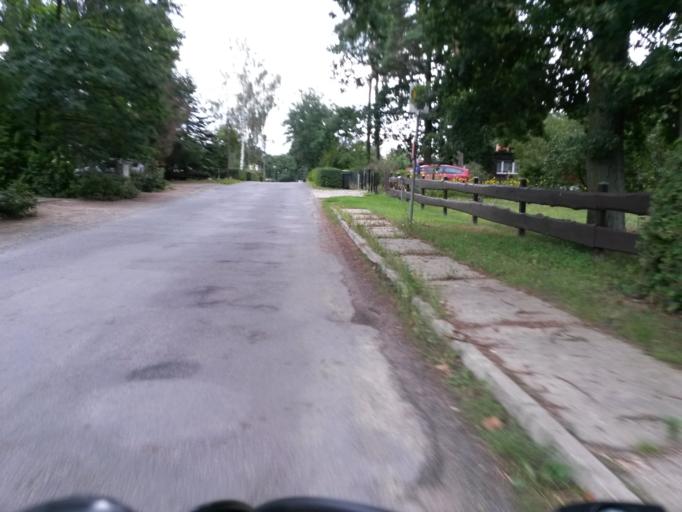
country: DE
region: Brandenburg
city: Angermunde
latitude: 53.0034
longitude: 13.9816
